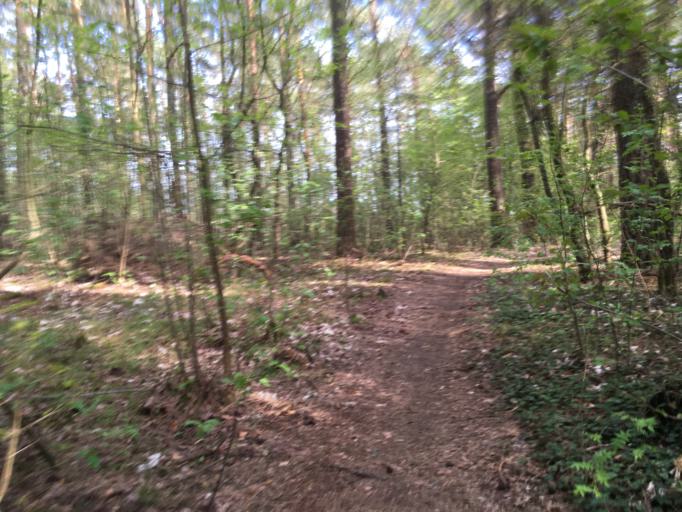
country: DE
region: Brandenburg
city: Bernau bei Berlin
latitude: 52.7053
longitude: 13.5794
